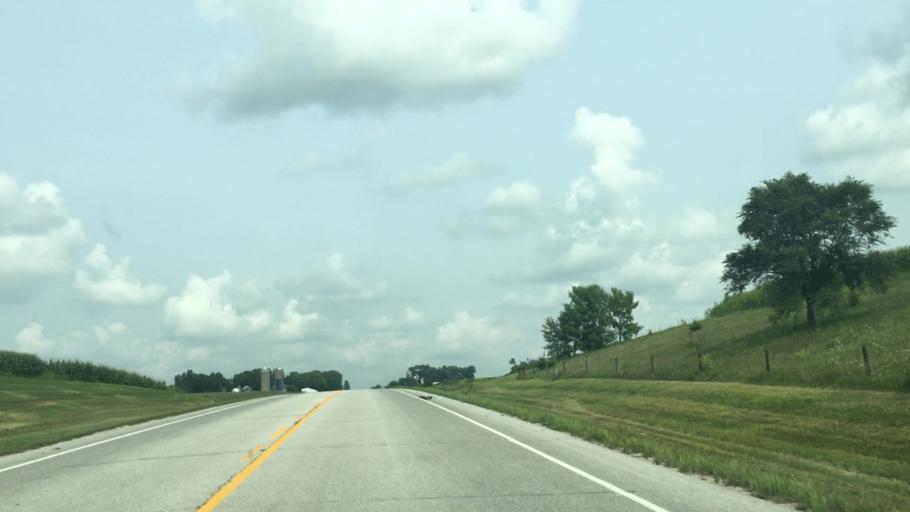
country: US
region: Minnesota
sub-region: Fillmore County
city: Harmony
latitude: 43.6083
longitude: -91.9297
